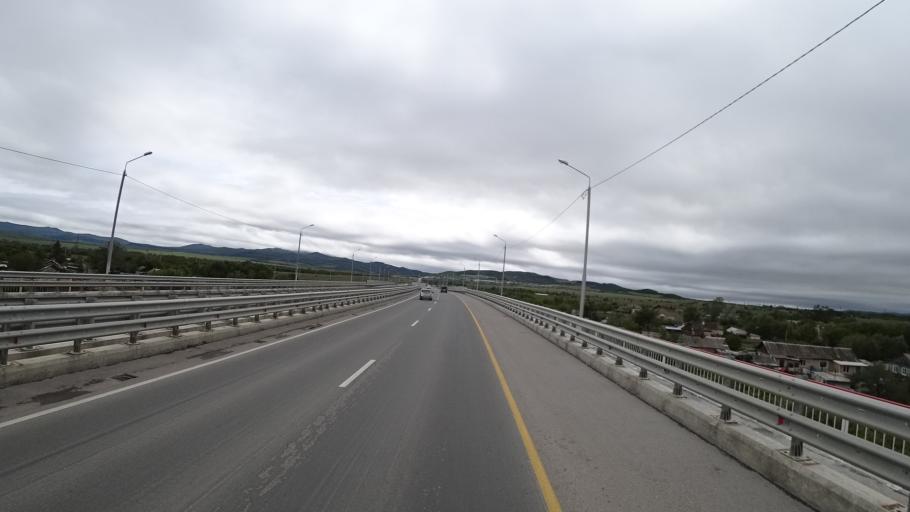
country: RU
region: Primorskiy
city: Monastyrishche
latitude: 44.1912
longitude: 132.4416
